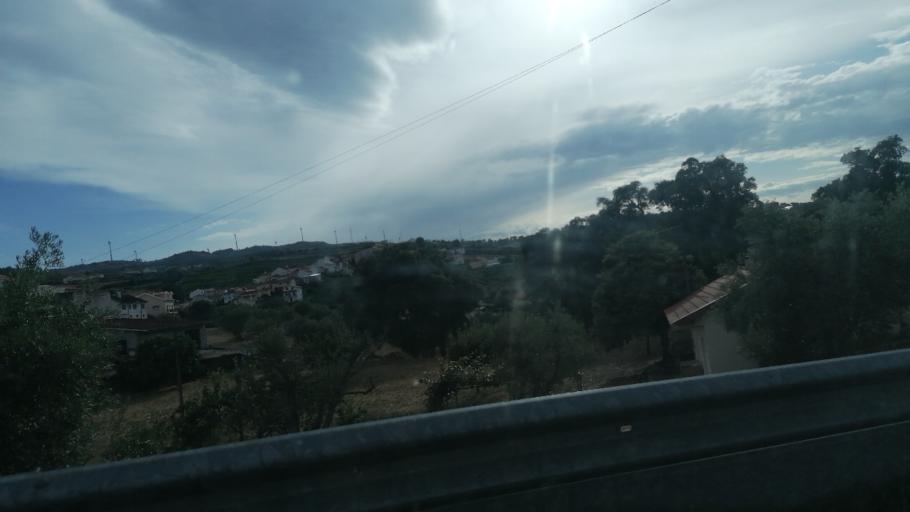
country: PT
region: Viseu
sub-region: Sao Joao da Pesqueira
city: Sao Joao da Pesqueira
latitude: 41.0720
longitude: -7.3911
